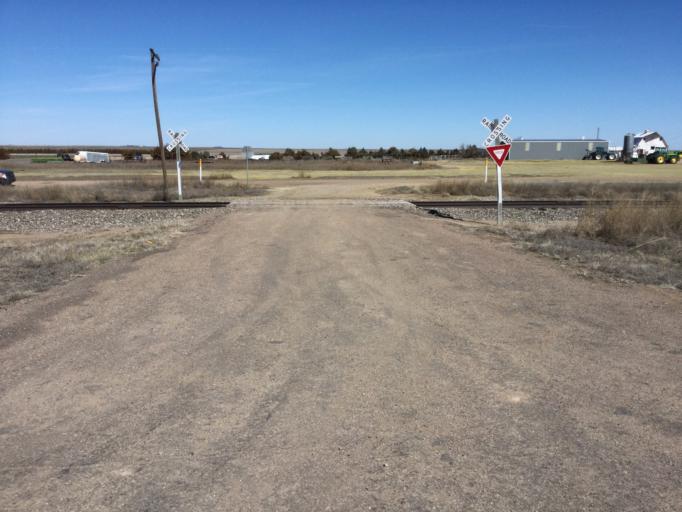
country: US
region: Kansas
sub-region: Greeley County
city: Tribune
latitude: 38.4666
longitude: -101.5856
